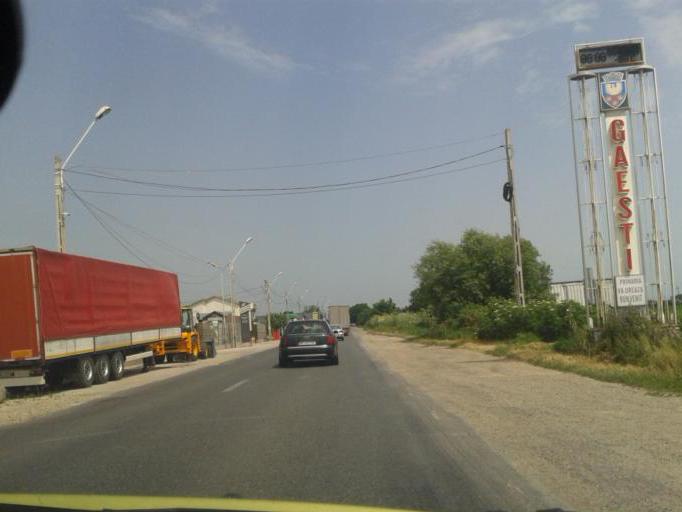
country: RO
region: Dambovita
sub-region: Oras Gaesti
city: Gaesti
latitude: 44.7033
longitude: 25.3106
